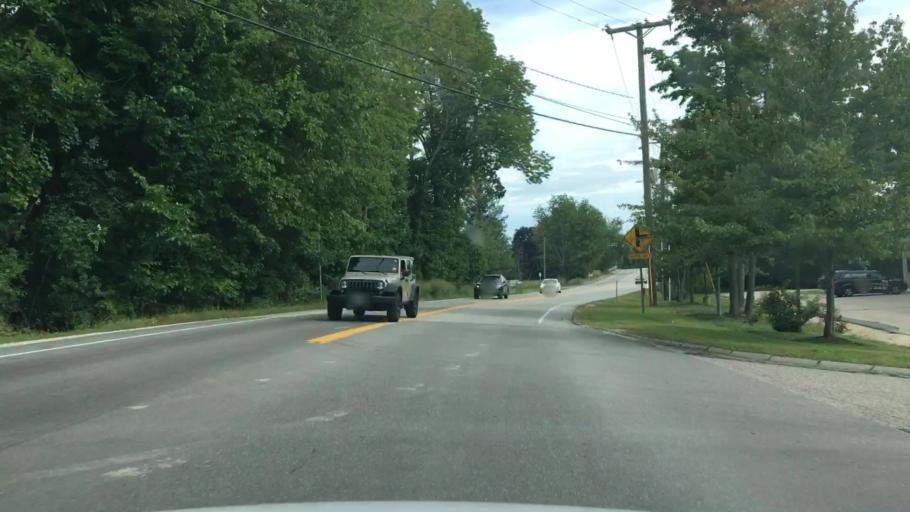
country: US
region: New Hampshire
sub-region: Strafford County
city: Dover
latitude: 43.1889
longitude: -70.9004
